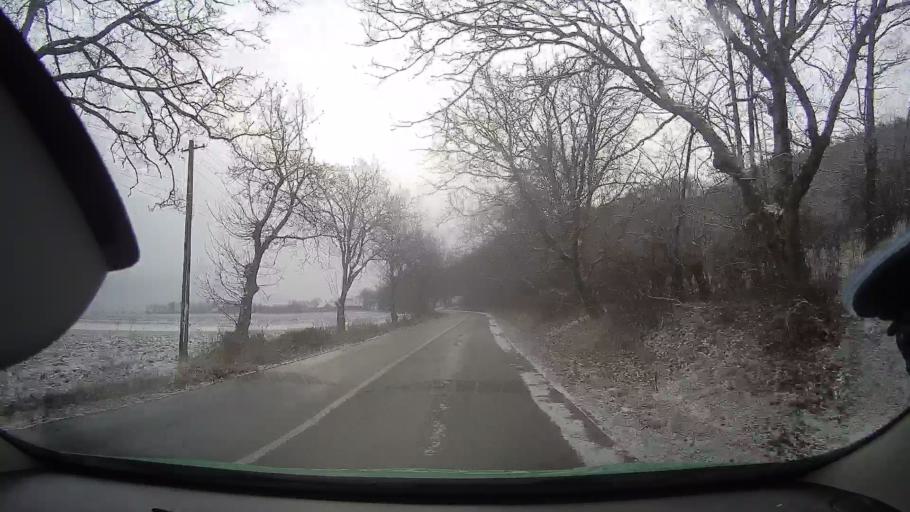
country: RO
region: Alba
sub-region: Comuna Rimetea
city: Rimetea
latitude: 46.4293
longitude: 23.5612
